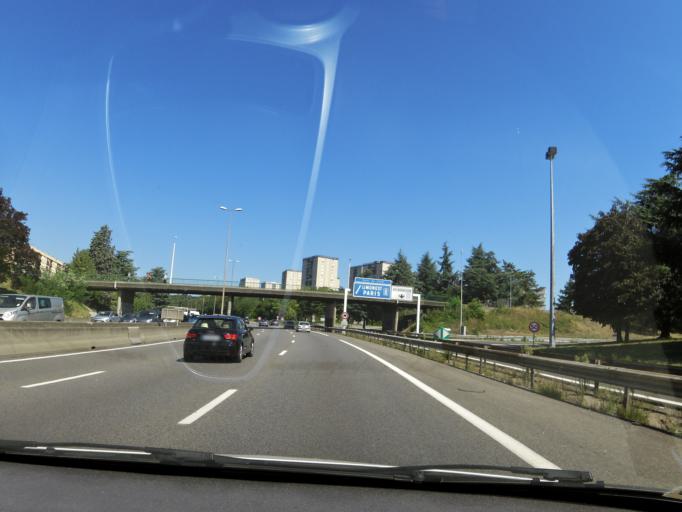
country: FR
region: Rhone-Alpes
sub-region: Departement du Rhone
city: Ecully
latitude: 45.7859
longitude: 4.7851
